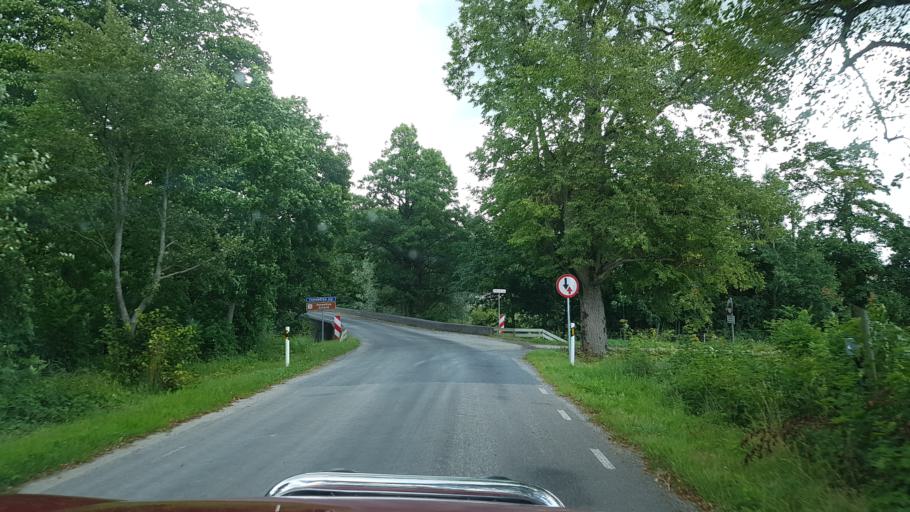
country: EE
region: Laeaene
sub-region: Lihula vald
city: Lihula
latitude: 58.7071
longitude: 24.0237
